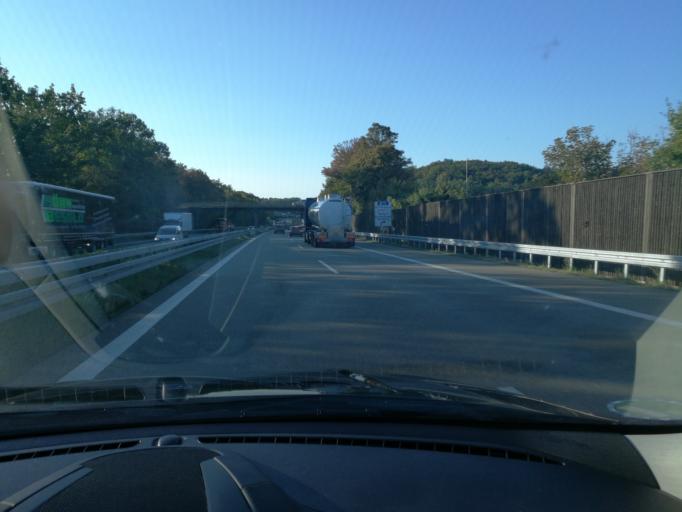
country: DE
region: Bavaria
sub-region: Upper Palatinate
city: Nittendorf
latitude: 49.0246
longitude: 11.9573
